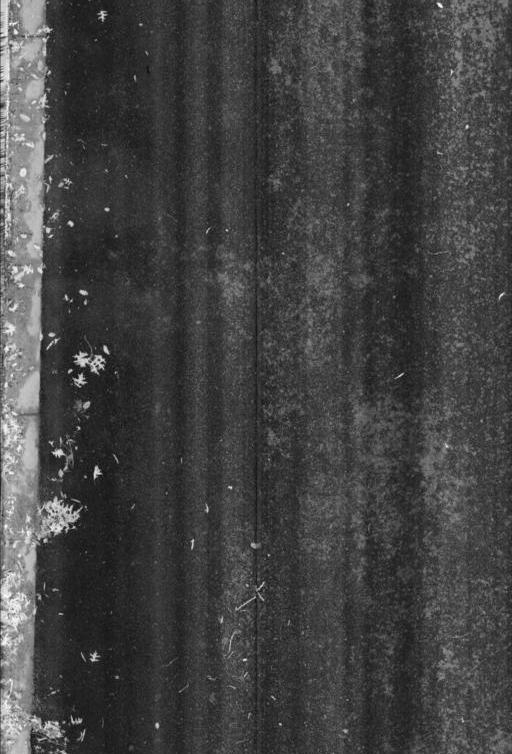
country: US
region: Maryland
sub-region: Prince George's County
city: Chillum
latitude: 38.9311
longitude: -76.9973
